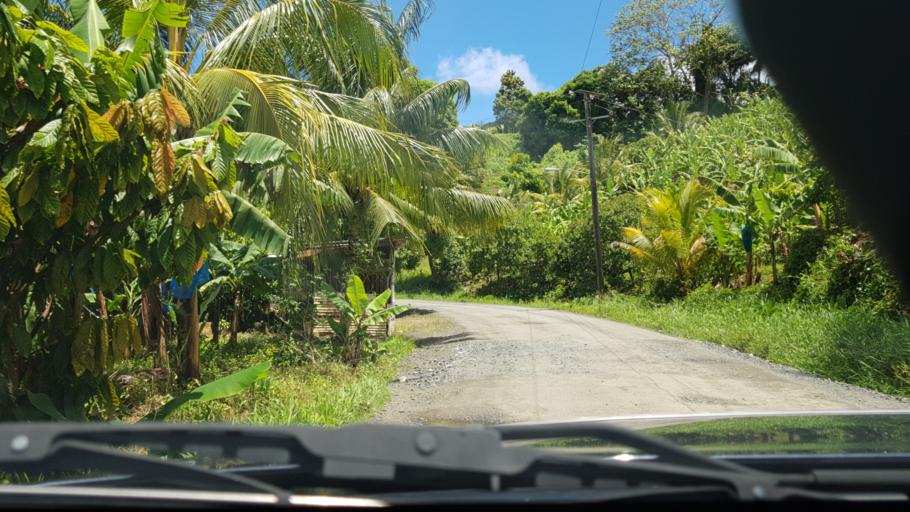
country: LC
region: Anse-la-Raye
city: Anse La Raye
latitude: 13.9484
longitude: -60.9918
